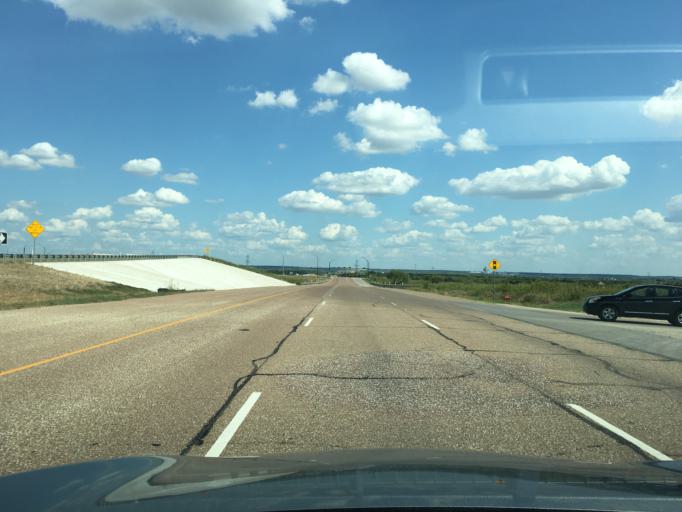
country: US
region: Texas
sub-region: Tarrant County
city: Mansfield
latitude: 32.5239
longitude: -97.0864
